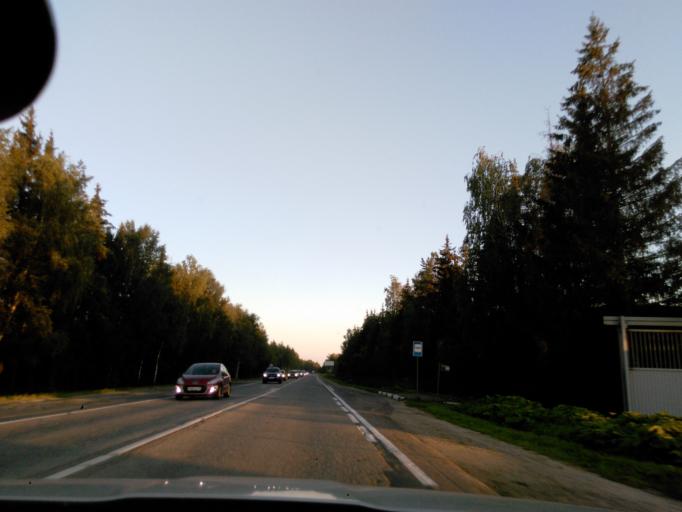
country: RU
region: Moskovskaya
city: Solnechnogorsk
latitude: 56.1052
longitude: 36.9126
